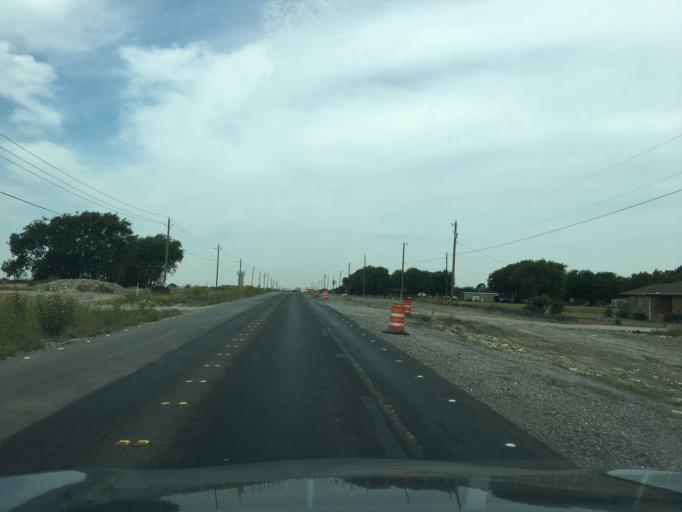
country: US
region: Texas
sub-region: Collin County
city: Parker
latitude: 33.0554
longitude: -96.6047
